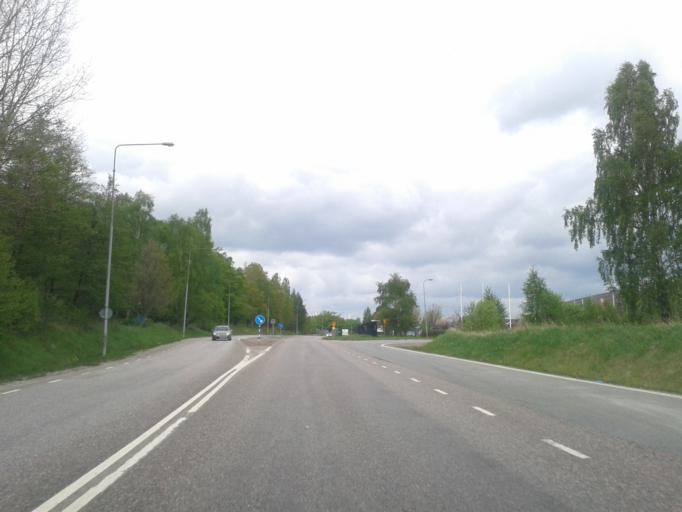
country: SE
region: Vaestra Goetaland
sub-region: Goteborg
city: Eriksbo
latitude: 57.7813
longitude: 12.0484
